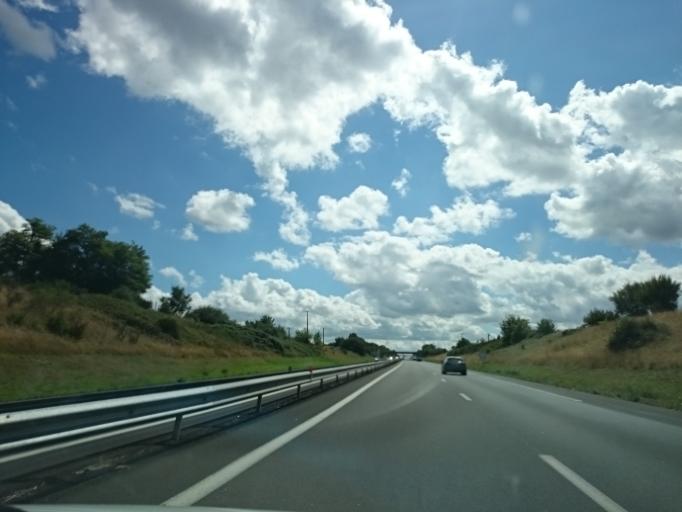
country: FR
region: Pays de la Loire
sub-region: Departement de Maine-et-Loire
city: Durtal
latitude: 47.6494
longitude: -0.2738
